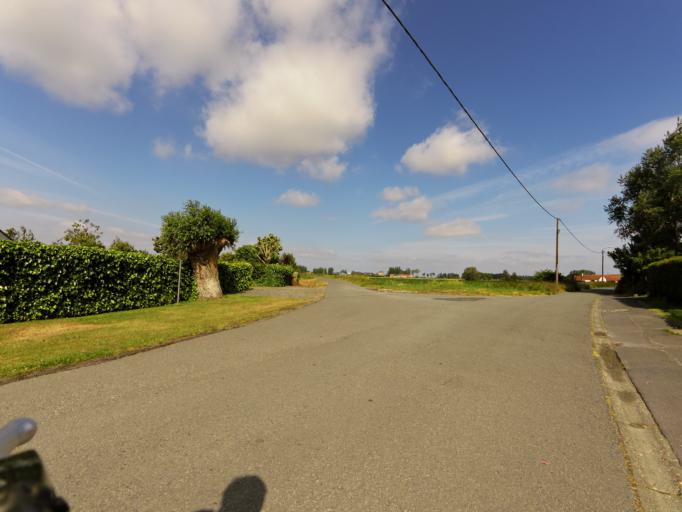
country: BE
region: Flanders
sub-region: Provincie West-Vlaanderen
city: Gistel
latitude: 51.1713
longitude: 2.9287
